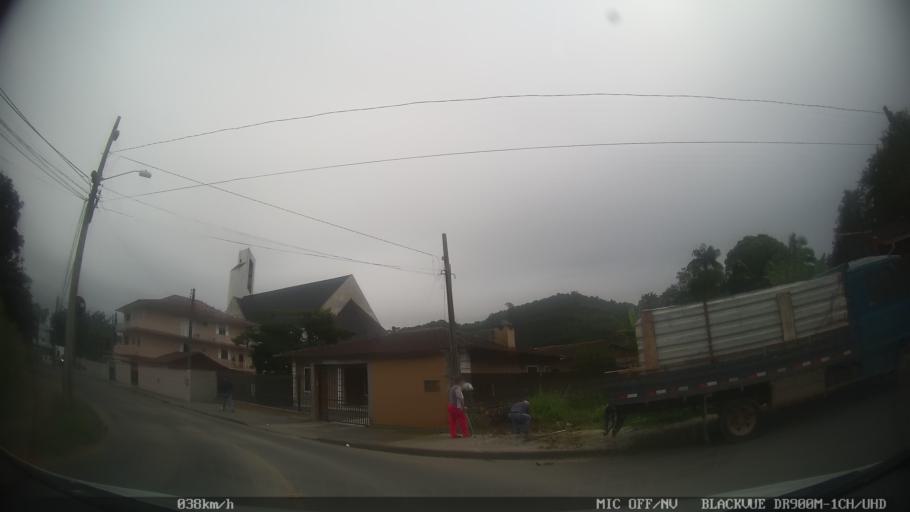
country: BR
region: Santa Catarina
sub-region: Joinville
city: Joinville
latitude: -26.2702
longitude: -48.8242
